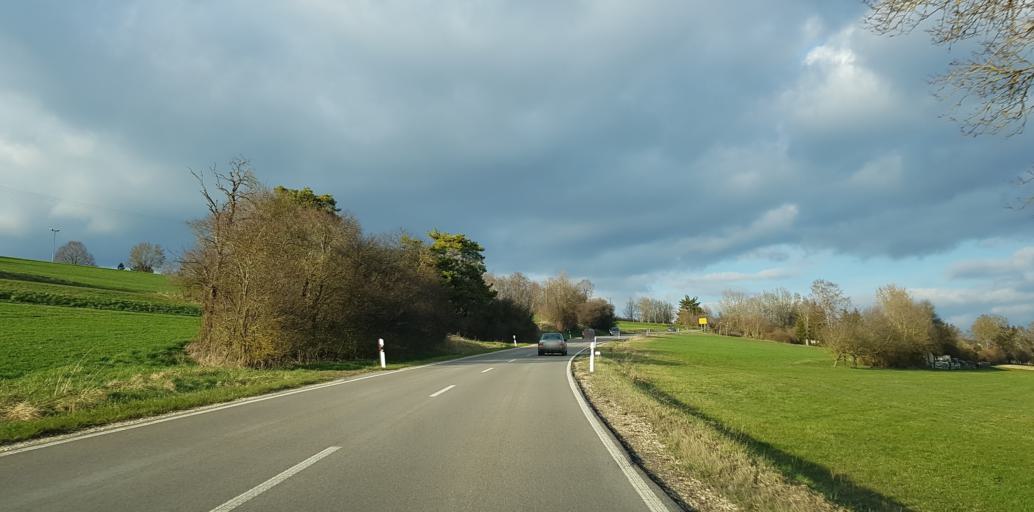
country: DE
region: Baden-Wuerttemberg
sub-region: Tuebingen Region
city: Erbach
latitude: 48.3739
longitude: 9.8836
